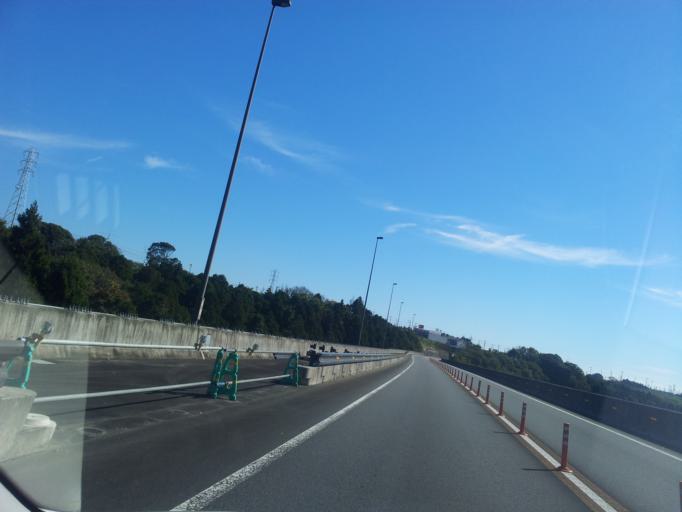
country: JP
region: Shizuoka
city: Kanaya
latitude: 34.8008
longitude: 138.1333
